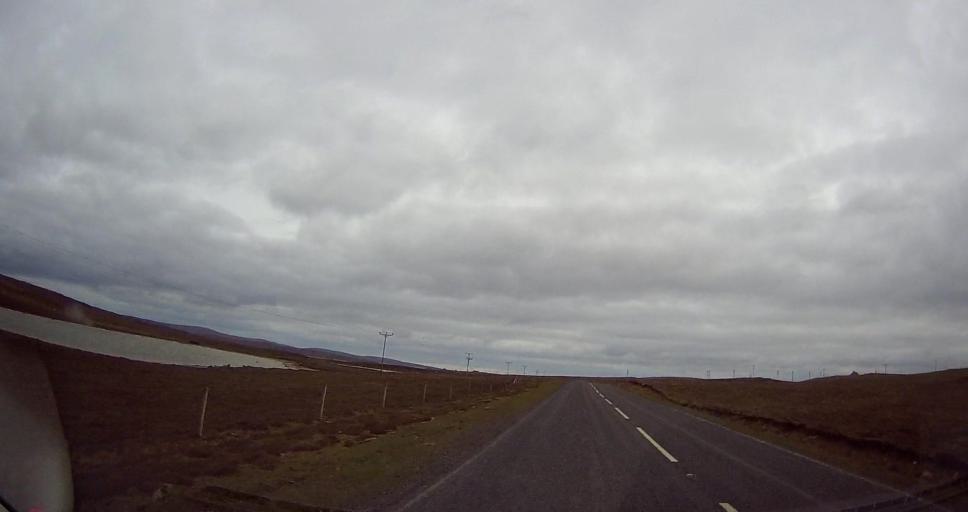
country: GB
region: Scotland
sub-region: Shetland Islands
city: Shetland
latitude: 60.7147
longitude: -0.9148
